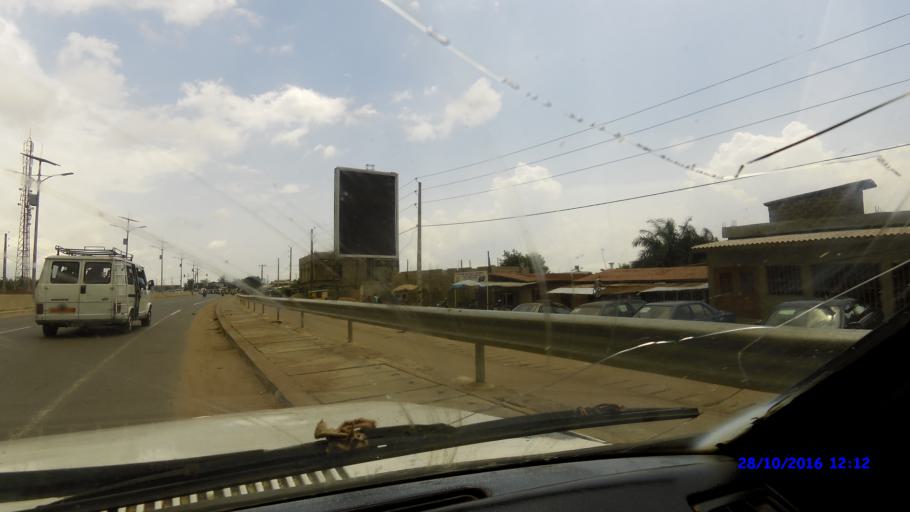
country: BJ
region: Atlantique
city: Hevie
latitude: 6.3876
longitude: 2.2786
